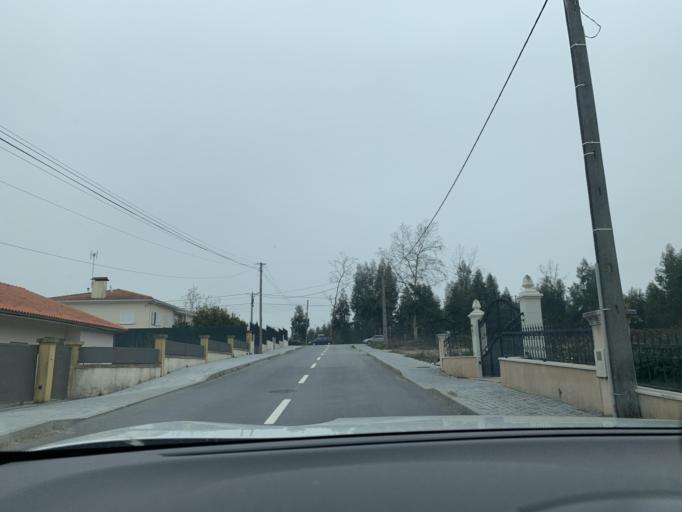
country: PT
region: Viseu
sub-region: Concelho de Tondela
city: Tondela
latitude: 40.5351
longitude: -8.0537
